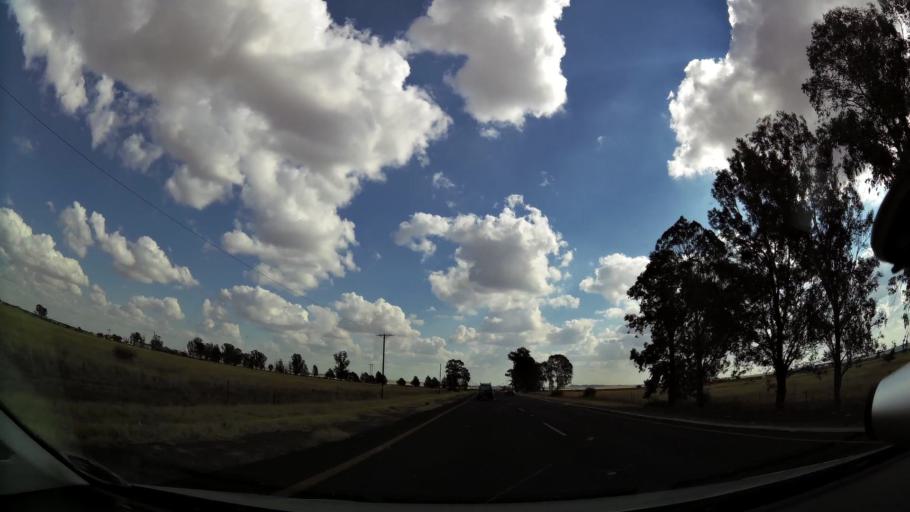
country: ZA
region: Orange Free State
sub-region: Xhariep District Municipality
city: Koffiefontein
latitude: -29.1314
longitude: 25.5290
